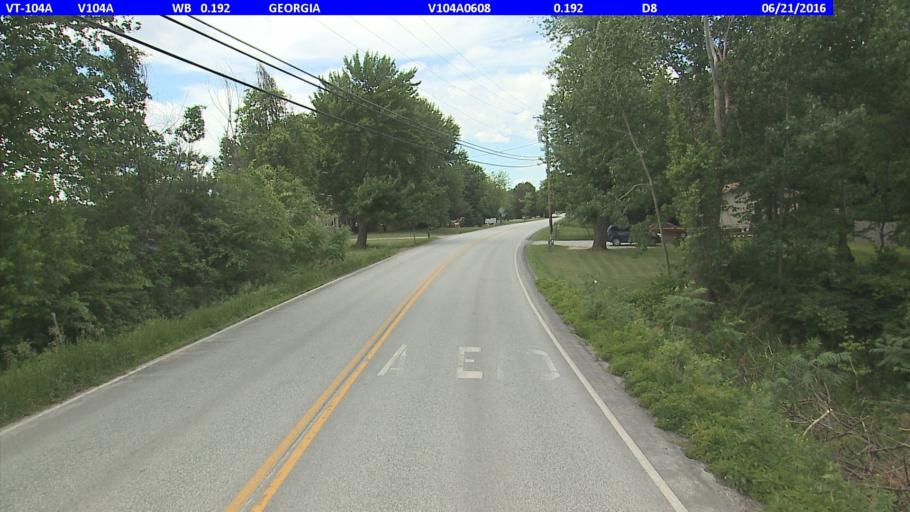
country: US
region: Vermont
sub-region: Chittenden County
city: Milton
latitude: 44.6929
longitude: -73.1050
